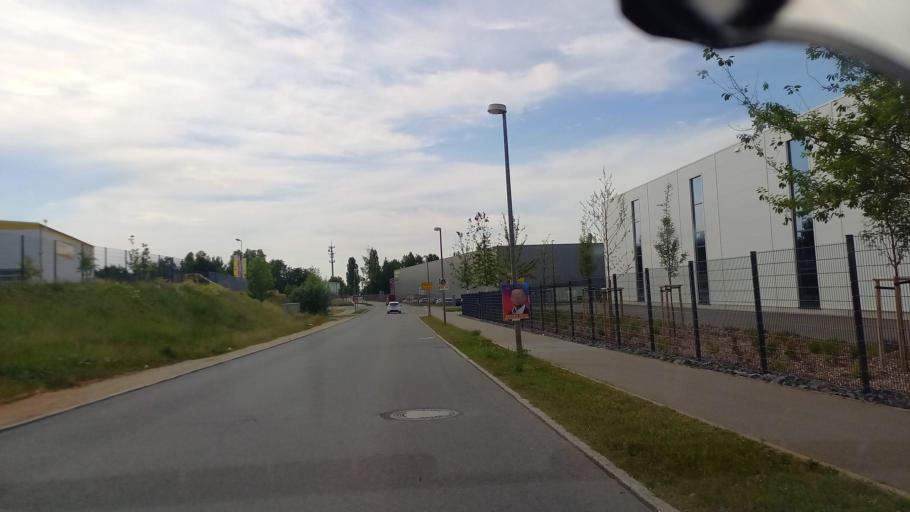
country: DE
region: Saxony
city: Reinsdorf
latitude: 50.6881
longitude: 12.5662
